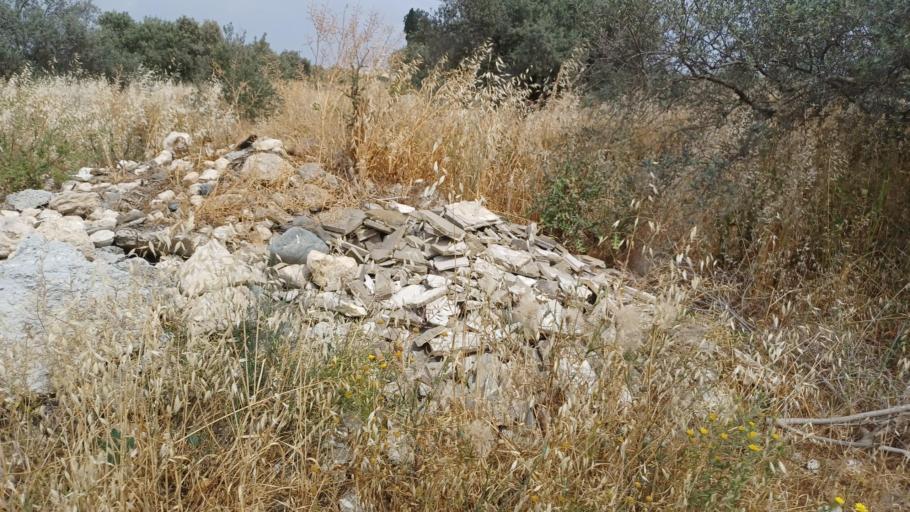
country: CY
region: Larnaka
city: Athienou
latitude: 35.0690
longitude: 33.5196
